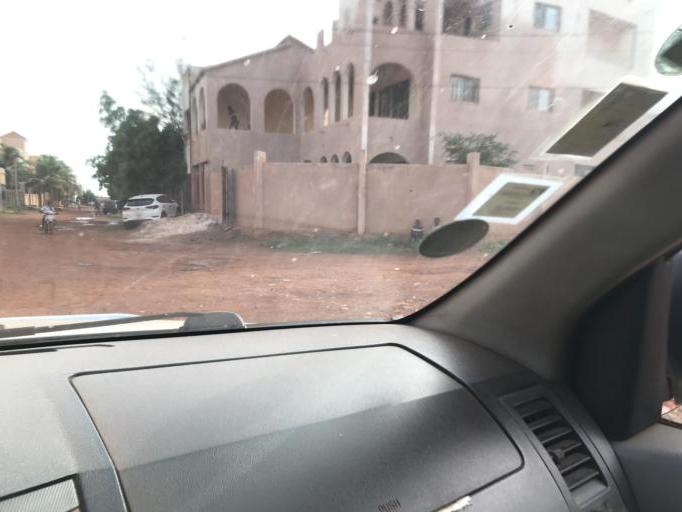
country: ML
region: Bamako
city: Bamako
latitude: 12.5863
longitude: -8.0051
